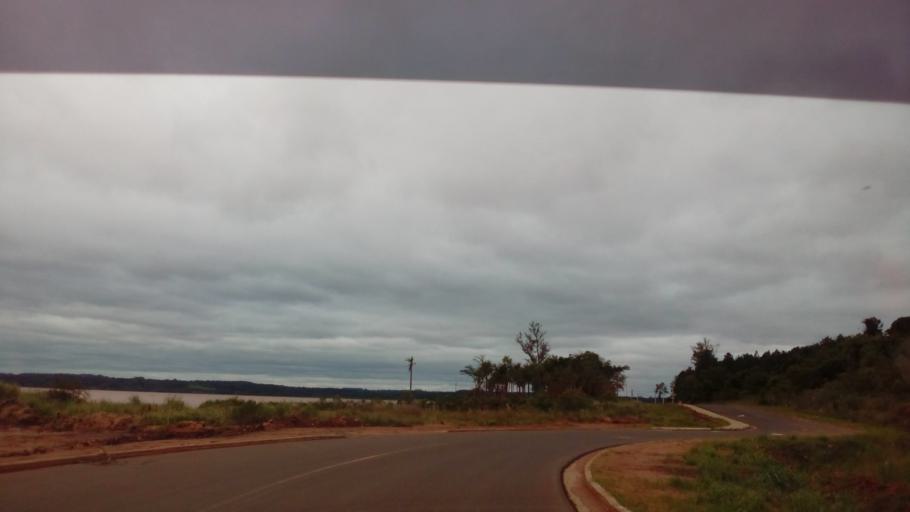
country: AR
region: Misiones
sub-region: Departamento de Candelaria
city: Candelaria
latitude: -27.4538
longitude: -55.7843
